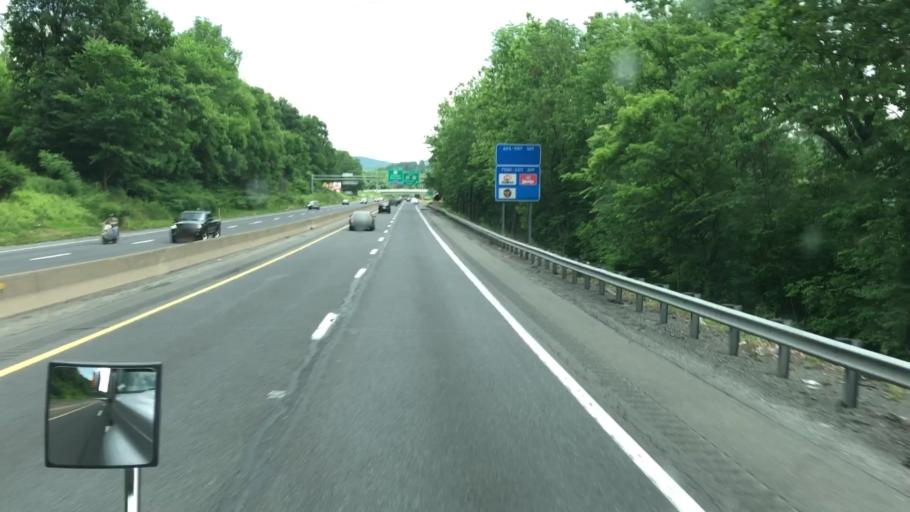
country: US
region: Pennsylvania
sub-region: Monroe County
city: East Stroudsburg
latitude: 40.9959
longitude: -75.1621
